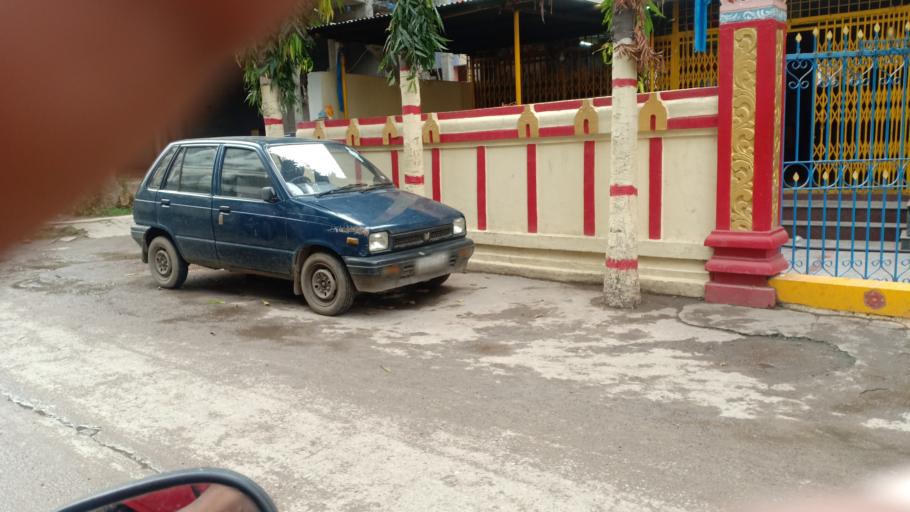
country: IN
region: Telangana
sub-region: Hyderabad
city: Hyderabad
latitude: 17.4322
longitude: 78.4420
